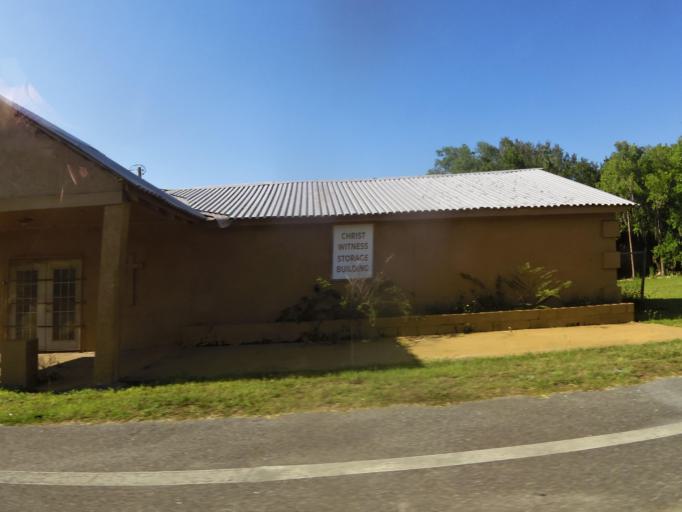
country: US
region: Florida
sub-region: Putnam County
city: Palatka
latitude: 29.6514
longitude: -81.6425
